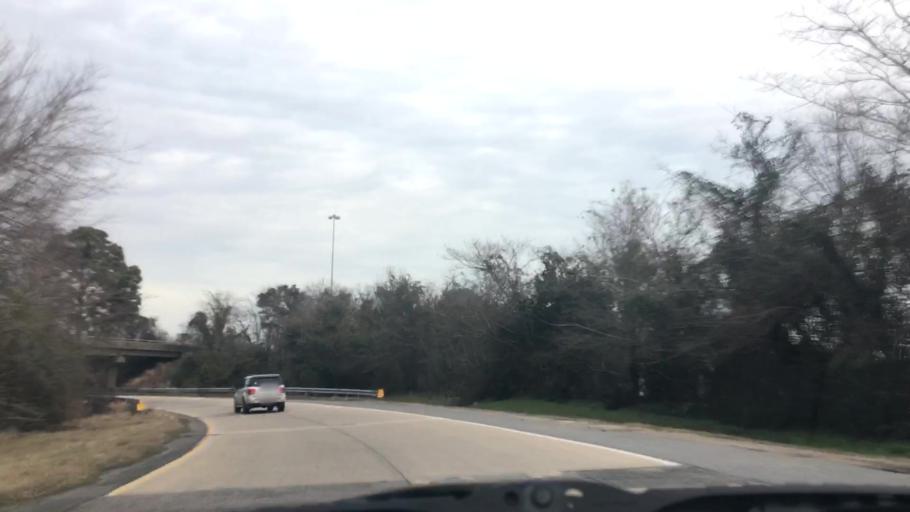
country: US
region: Virginia
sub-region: City of Norfolk
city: Norfolk
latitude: 36.9035
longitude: -76.2552
